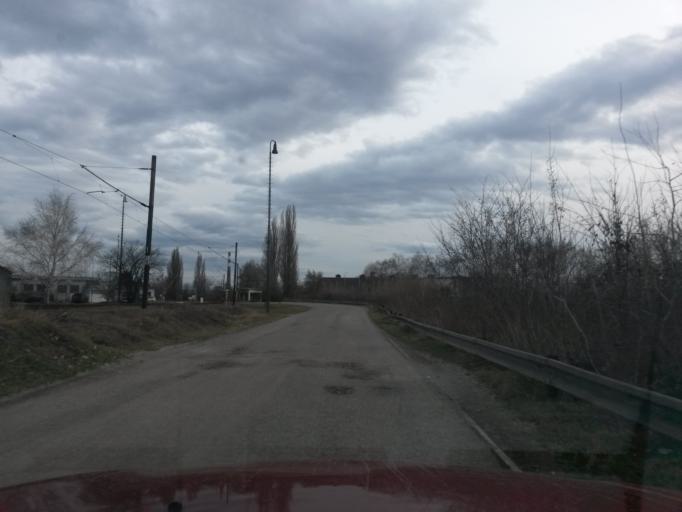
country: SK
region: Kosicky
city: Kosice
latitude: 48.7162
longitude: 21.2711
